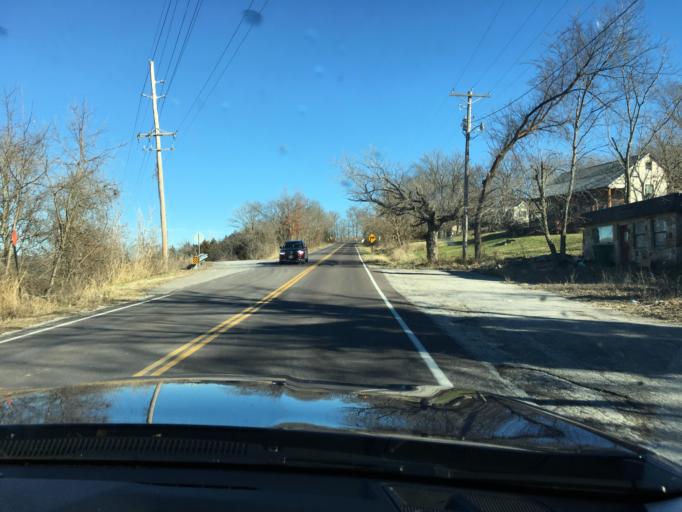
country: US
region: Missouri
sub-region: Jefferson County
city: De Soto
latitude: 38.1512
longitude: -90.5466
